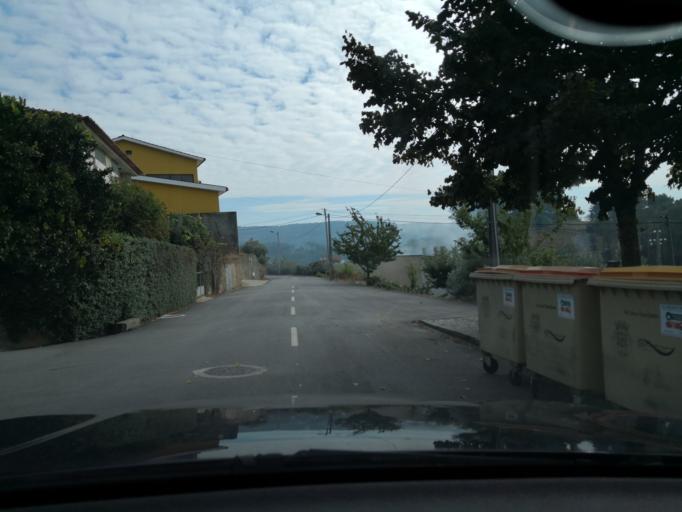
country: PT
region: Vila Real
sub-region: Sabrosa
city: Vilela
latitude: 41.2235
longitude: -7.6931
